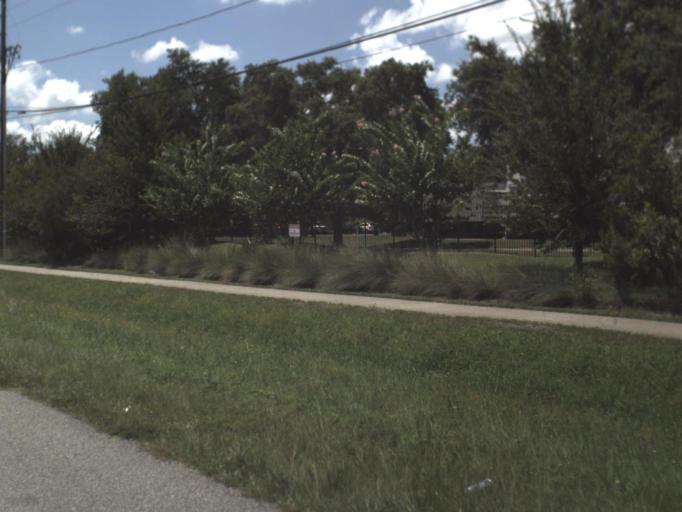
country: US
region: Florida
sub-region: Pinellas County
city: South Highpoint
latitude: 27.9043
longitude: -82.7293
